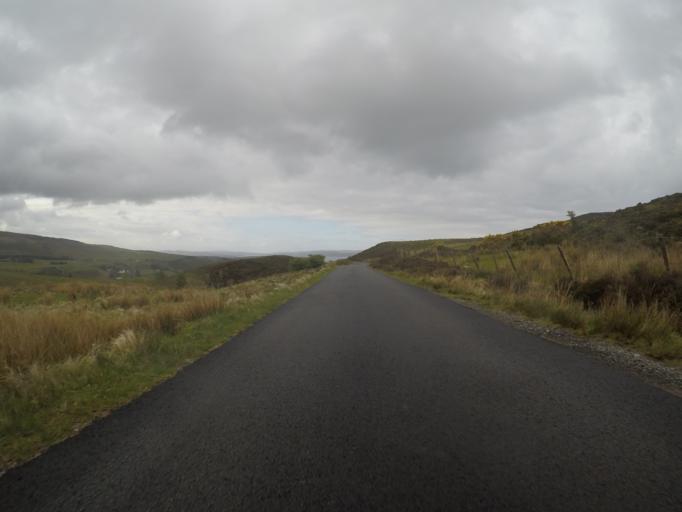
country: GB
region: Scotland
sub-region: Highland
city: Portree
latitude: 57.5973
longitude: -6.3571
